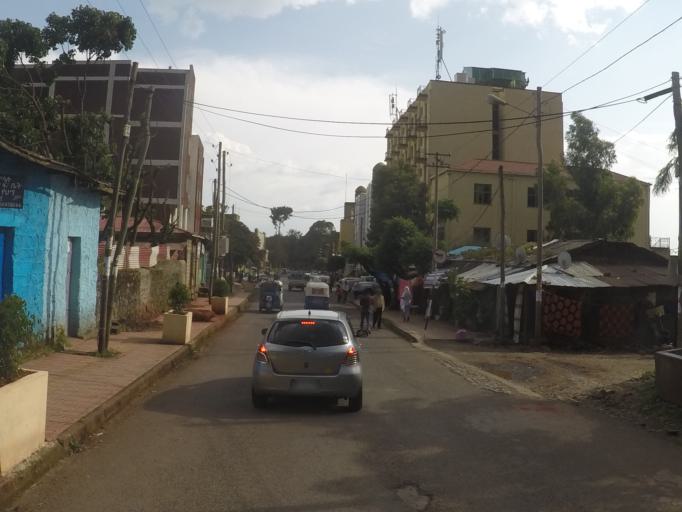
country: ET
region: Amhara
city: Gondar
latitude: 12.6168
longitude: 37.4725
